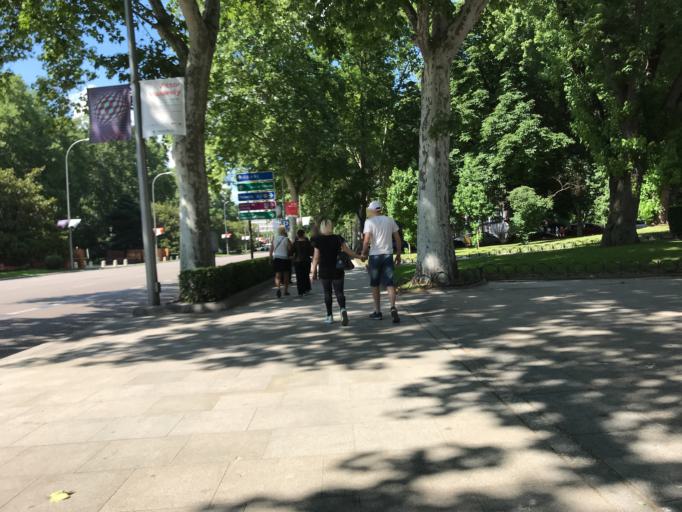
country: ES
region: Madrid
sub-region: Provincia de Madrid
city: Madrid
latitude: 40.4164
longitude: -3.6934
